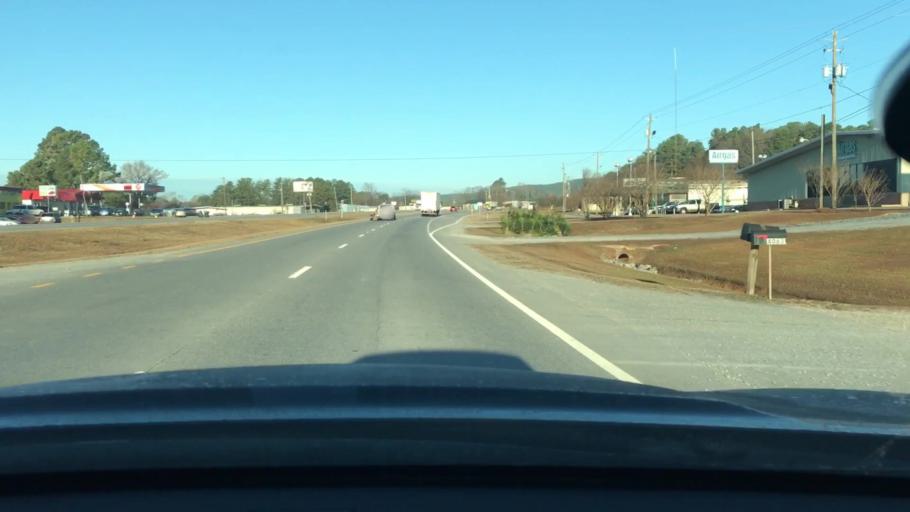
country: US
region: Alabama
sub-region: Talladega County
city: Mignon
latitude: 33.1785
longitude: -86.2957
